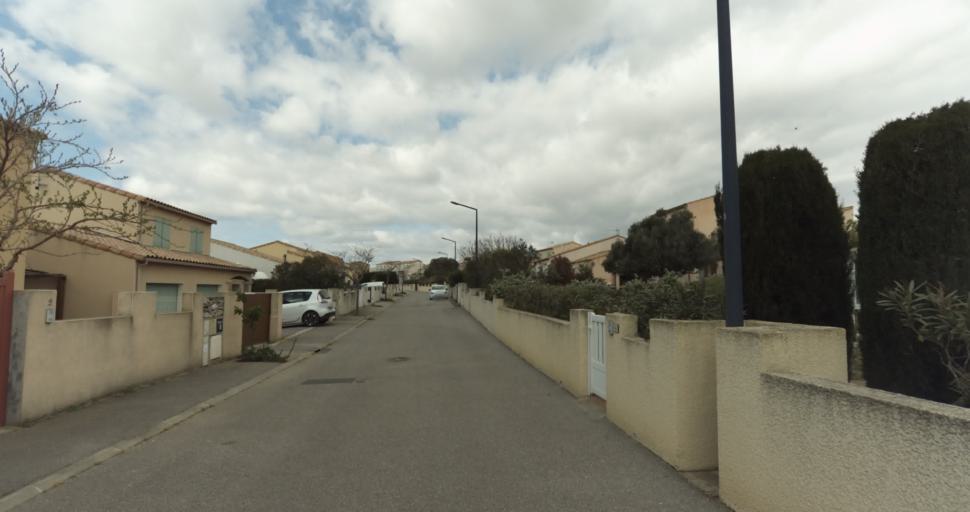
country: FR
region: Languedoc-Roussillon
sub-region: Departement de l'Aude
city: Leucate
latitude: 42.9058
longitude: 3.0315
